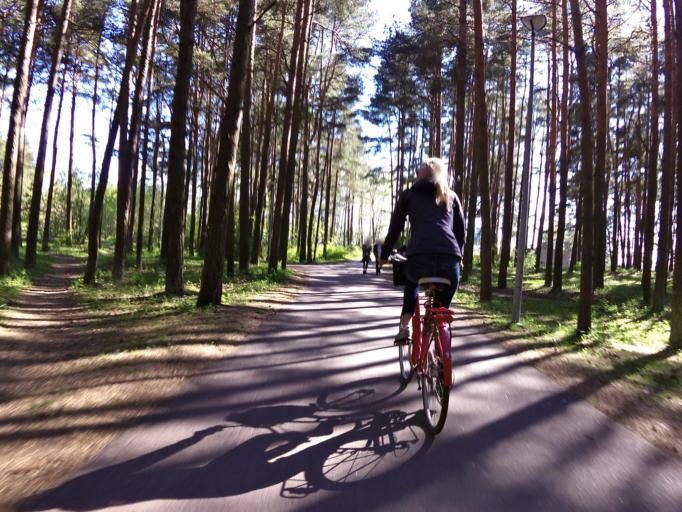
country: EE
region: Harju
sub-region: Viimsi vald
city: Viimsi
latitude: 59.4693
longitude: 24.8305
